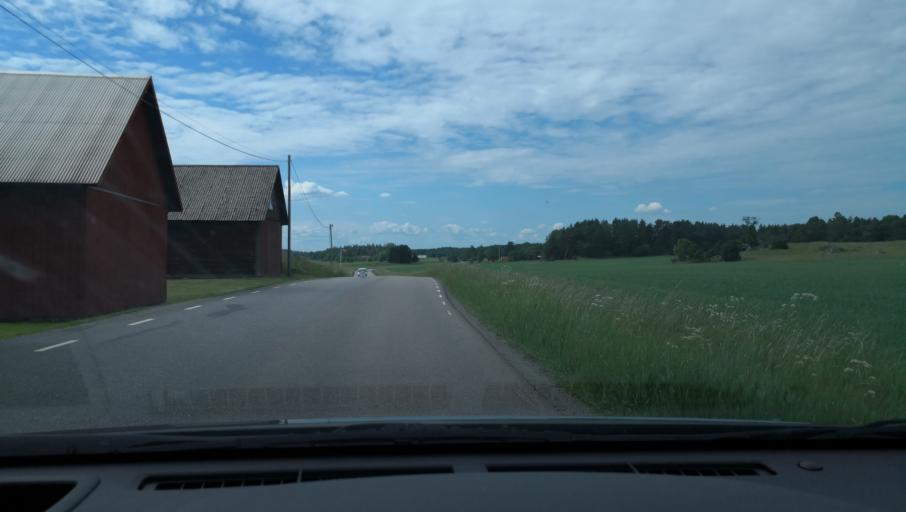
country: SE
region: Uppsala
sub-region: Uppsala Kommun
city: Uppsala
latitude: 59.8129
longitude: 17.5070
